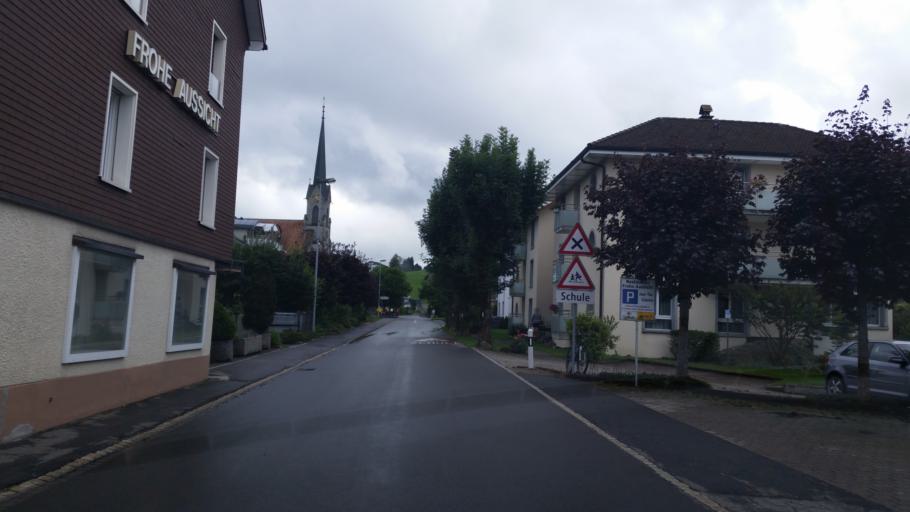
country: CH
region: Schwyz
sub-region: Bezirk Einsiedeln
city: Einsiedeln
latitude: 47.1496
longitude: 8.7283
